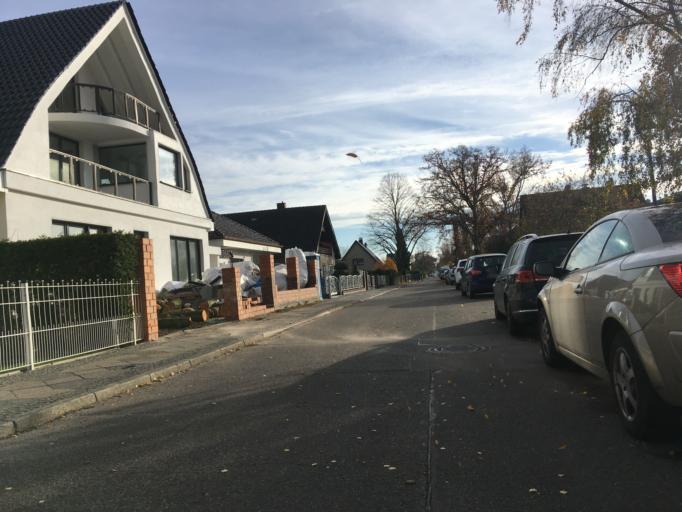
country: DE
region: Berlin
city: Rudow
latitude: 52.4378
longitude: 13.4770
